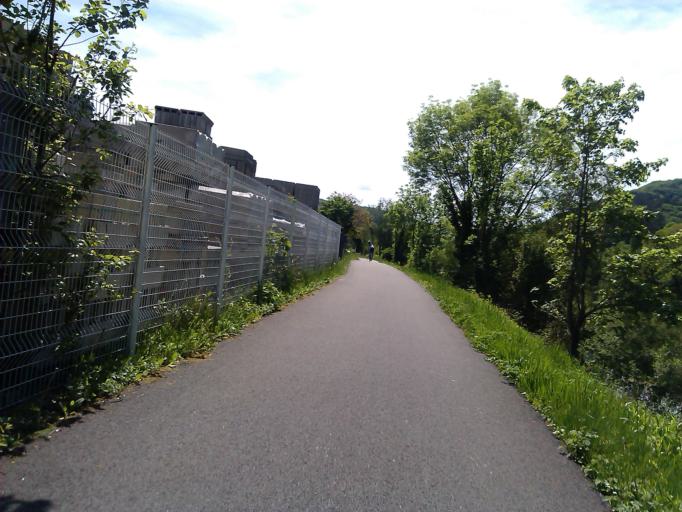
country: FR
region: Franche-Comte
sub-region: Departement du Doubs
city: Beure
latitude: 47.2141
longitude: 6.0014
